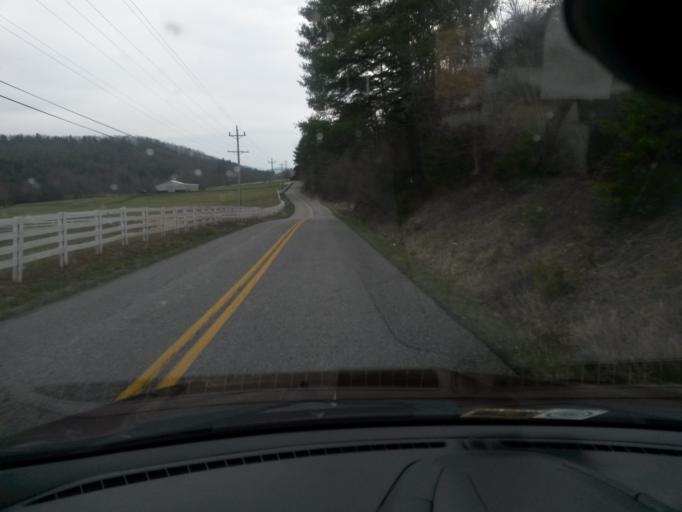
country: US
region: Virginia
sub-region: Bath County
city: Warm Springs
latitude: 37.9891
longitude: -79.8977
